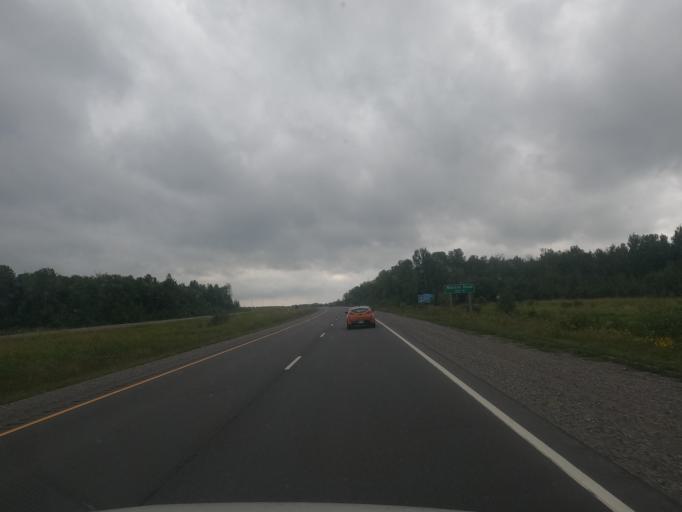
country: CA
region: Ontario
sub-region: Algoma
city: Sault Ste. Marie
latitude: 46.4751
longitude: -84.0556
